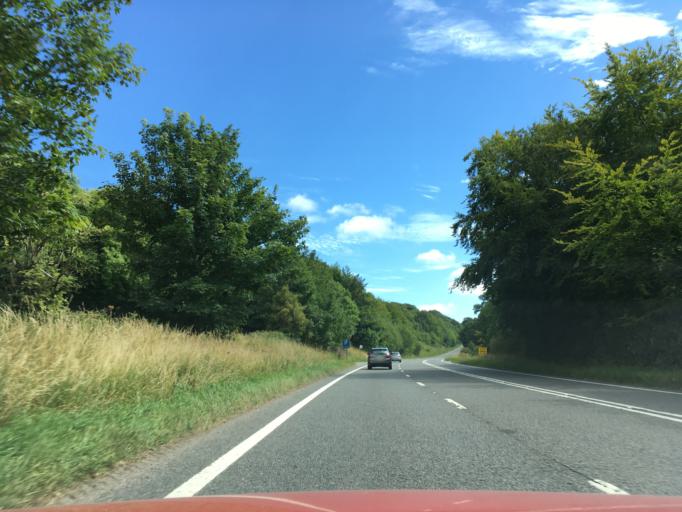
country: GB
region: England
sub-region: Somerset
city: Yeovil
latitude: 50.8522
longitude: -2.5848
